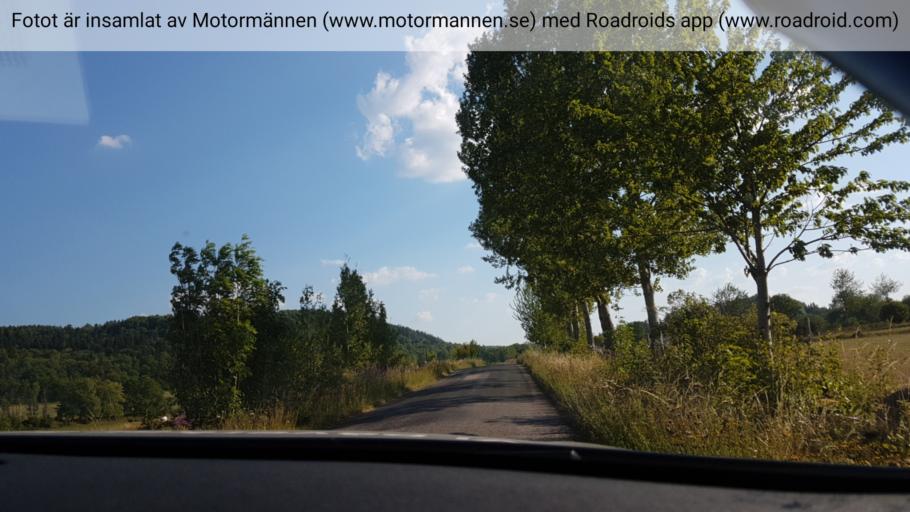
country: SE
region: Vaestra Goetaland
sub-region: Skovde Kommun
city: Stopen
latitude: 58.4745
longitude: 13.7474
